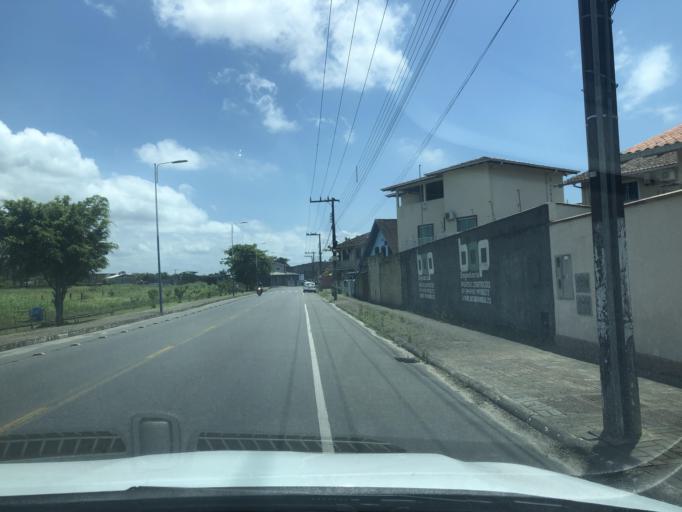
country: BR
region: Santa Catarina
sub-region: Sao Francisco Do Sul
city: Sao Francisco do Sul
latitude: -26.2492
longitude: -48.6394
